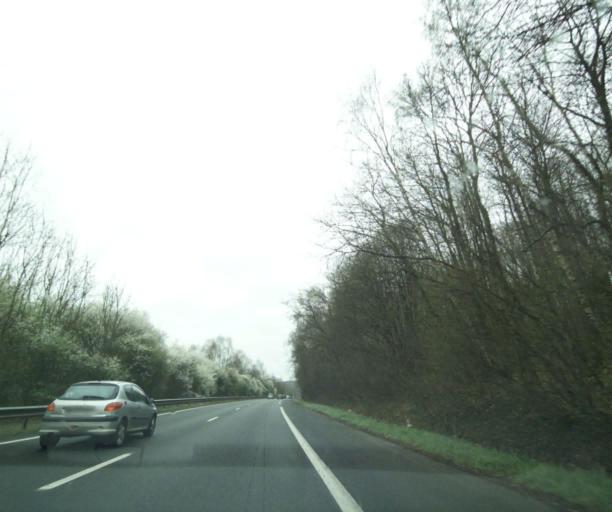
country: FR
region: Ile-de-France
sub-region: Departement de l'Essonne
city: Marcoussis
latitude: 48.6435
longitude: 2.1967
